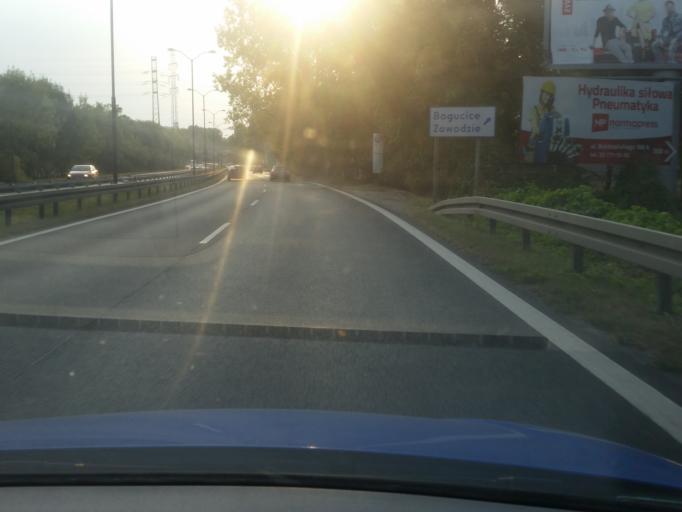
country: PL
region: Silesian Voivodeship
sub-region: Katowice
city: Katowice
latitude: 50.2632
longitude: 19.0585
